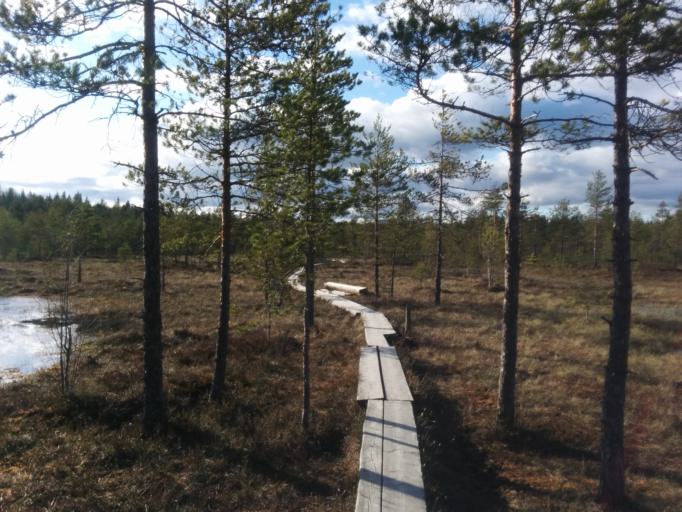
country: FI
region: Haeme
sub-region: Riihimaeki
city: Riihimaeki
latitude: 60.7601
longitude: 24.8252
